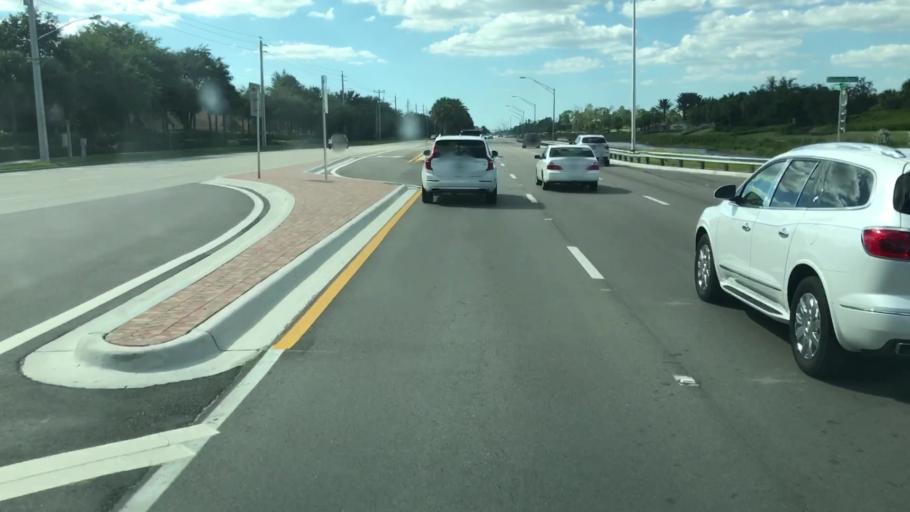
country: US
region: Florida
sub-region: Collier County
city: Vineyards
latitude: 26.2731
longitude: -81.6935
